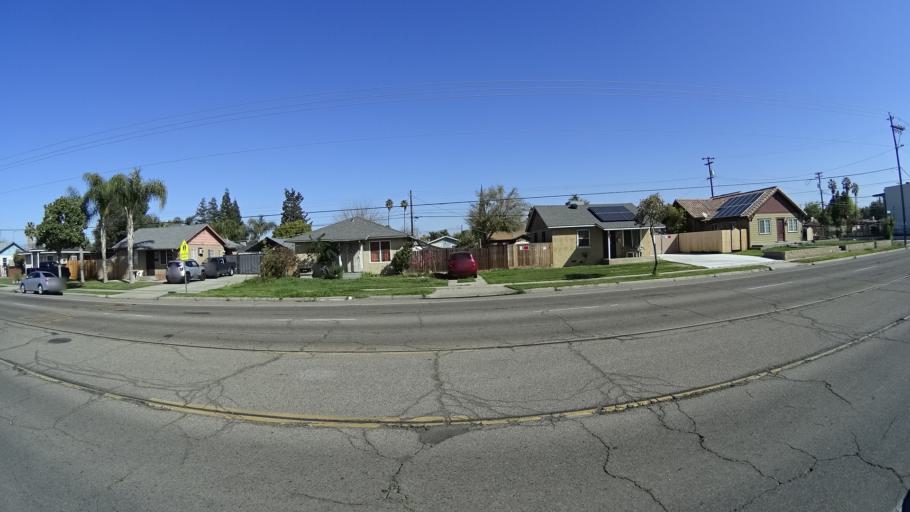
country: US
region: California
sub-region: Fresno County
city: Fresno
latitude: 36.7792
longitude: -119.8295
